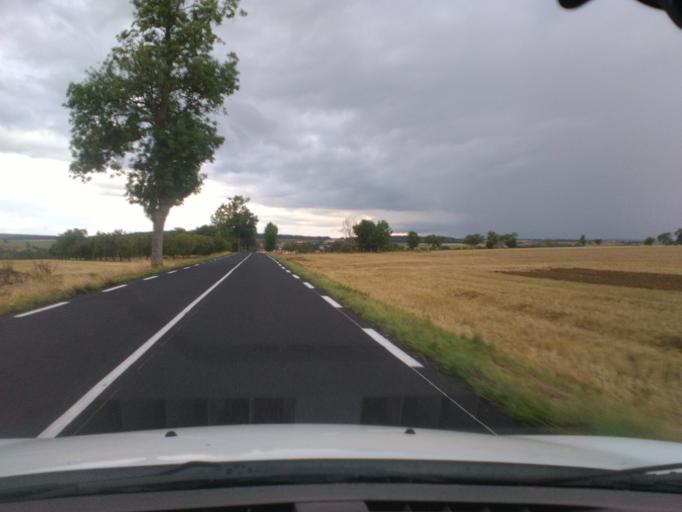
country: FR
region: Lorraine
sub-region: Departement de Meurthe-et-Moselle
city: Vezelise
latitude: 48.4051
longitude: 6.1356
